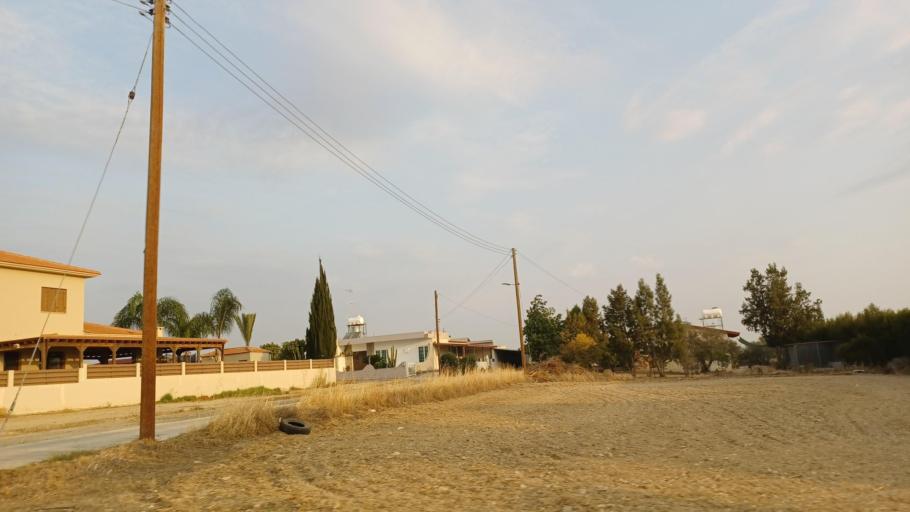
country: CY
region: Larnaka
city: Athienou
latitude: 35.0658
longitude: 33.5294
